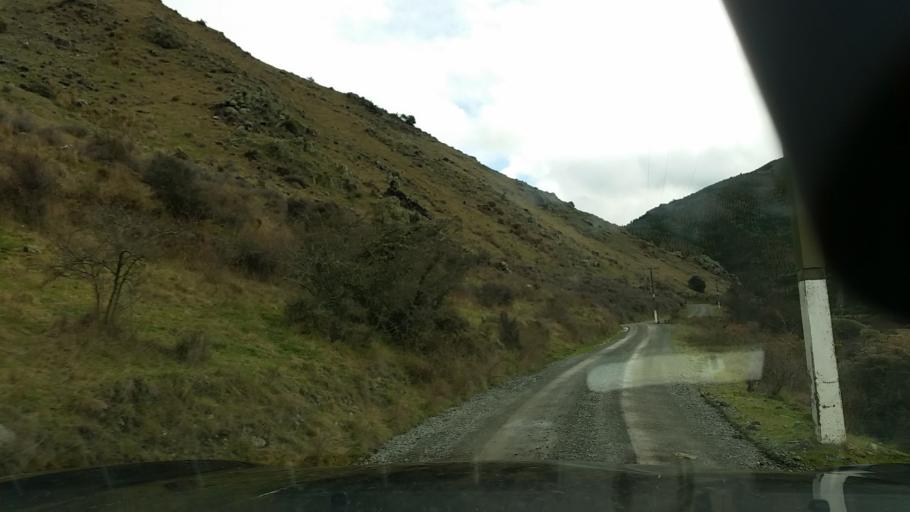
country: NZ
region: Tasman
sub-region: Tasman District
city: Richmond
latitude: -41.7317
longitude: 173.4488
